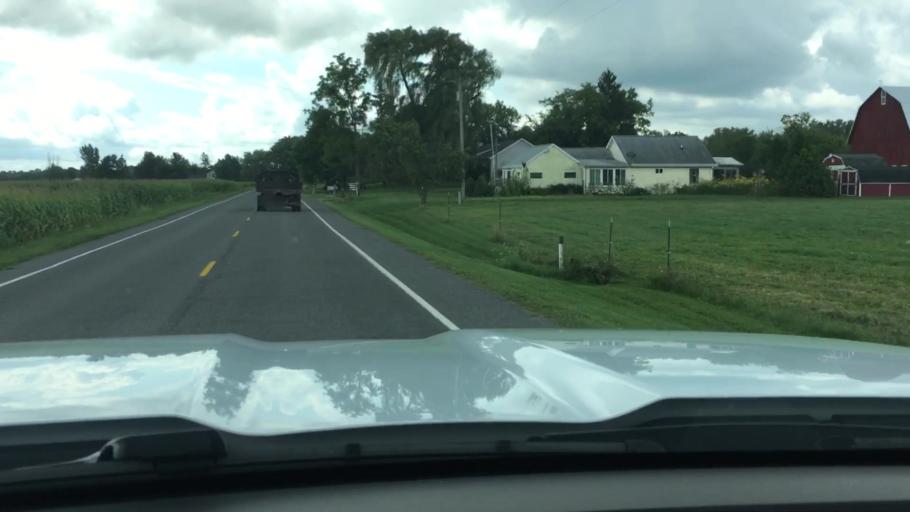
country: US
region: Michigan
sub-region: Eaton County
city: Eaton Rapids
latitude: 42.5436
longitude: -84.5621
